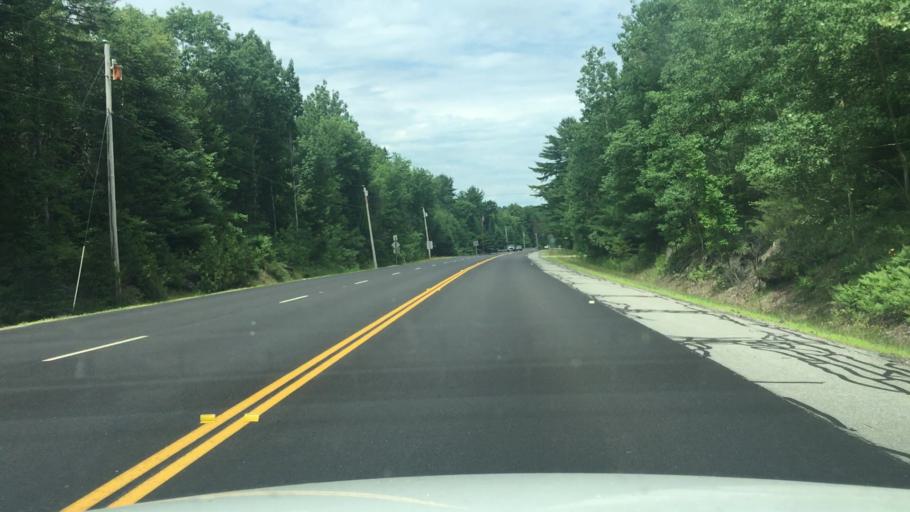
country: US
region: Maine
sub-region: Waldo County
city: Palermo
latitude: 44.3988
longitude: -69.4751
